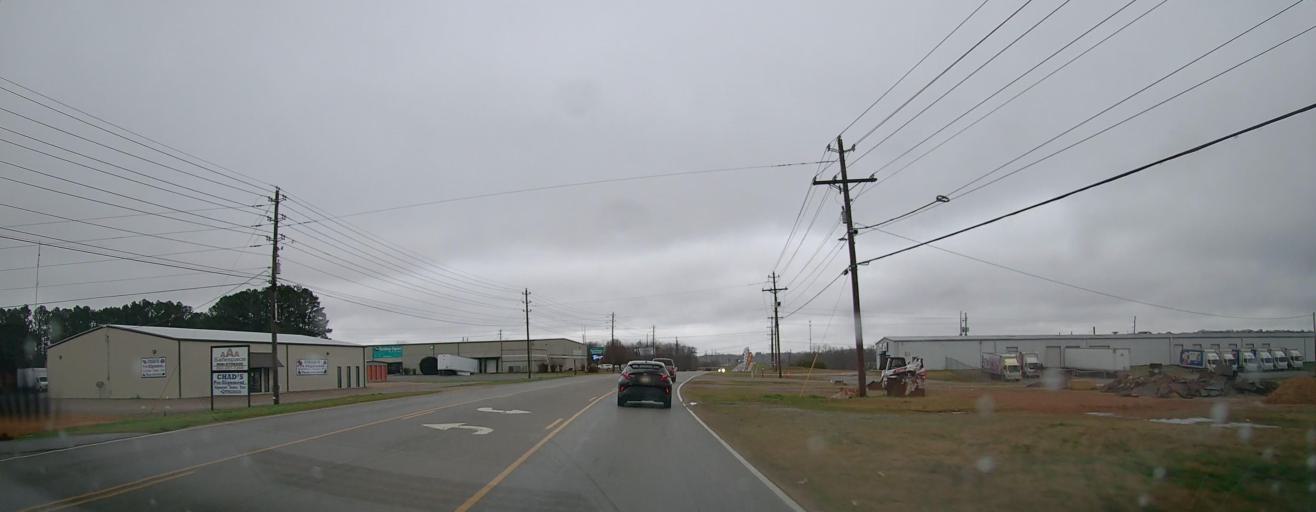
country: US
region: Mississippi
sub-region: Alcorn County
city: Corinth
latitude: 34.9090
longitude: -88.5213
